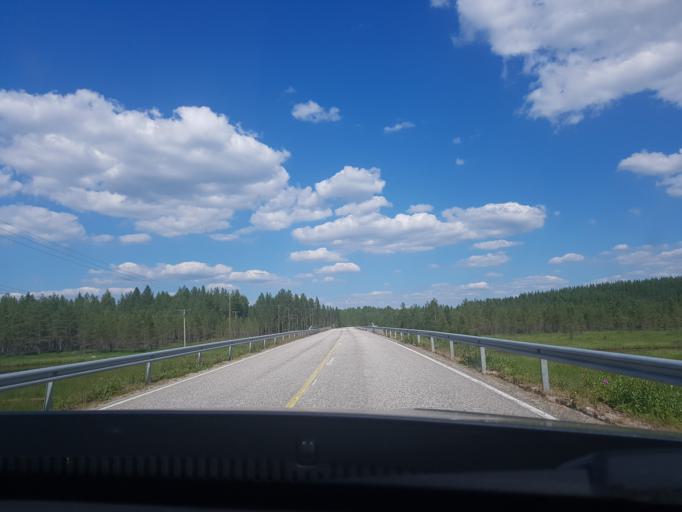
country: FI
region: Kainuu
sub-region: Kehys-Kainuu
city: Kuhmo
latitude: 64.2218
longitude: 29.7995
